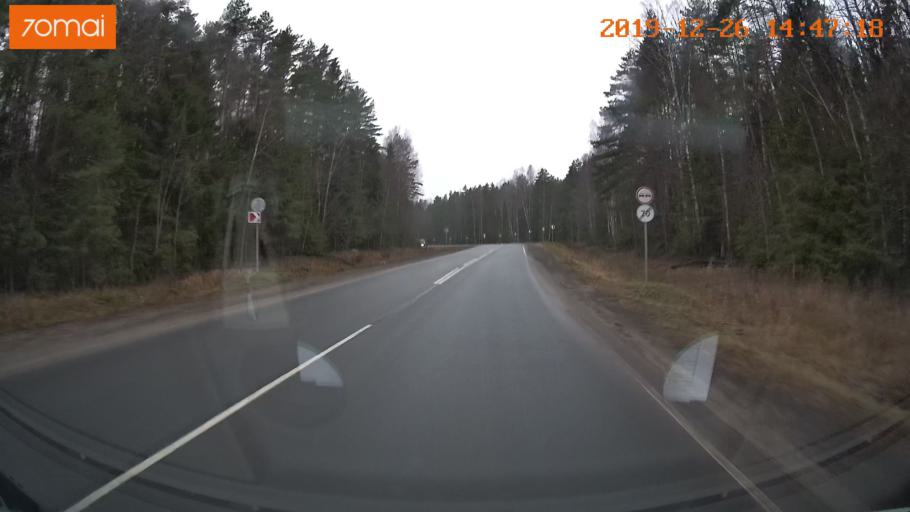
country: RU
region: Jaroslavl
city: Poshekhon'ye
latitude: 58.3416
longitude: 39.0011
